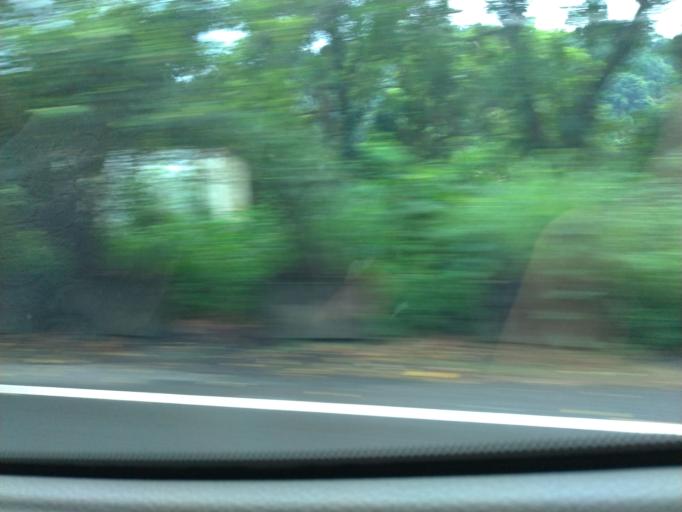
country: TW
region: Taipei
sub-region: Taipei
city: Banqiao
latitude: 24.9284
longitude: 121.4235
